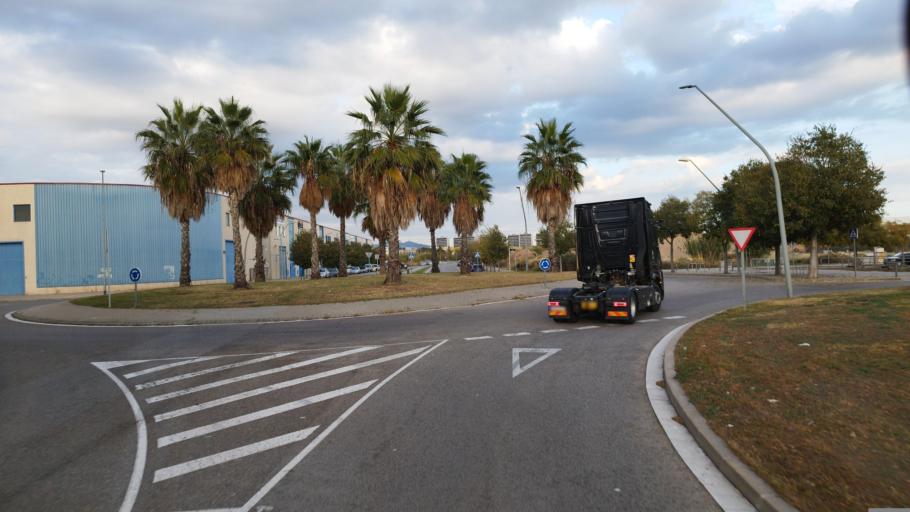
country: ES
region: Catalonia
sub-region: Provincia de Barcelona
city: Viladecans
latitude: 41.3031
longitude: 2.0155
